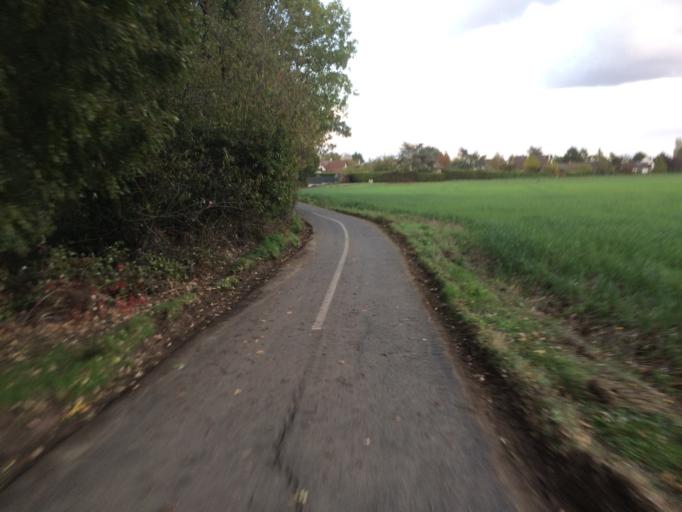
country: FR
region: Ile-de-France
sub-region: Departement de l'Essonne
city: Les Ulis
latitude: 48.6754
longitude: 2.1553
